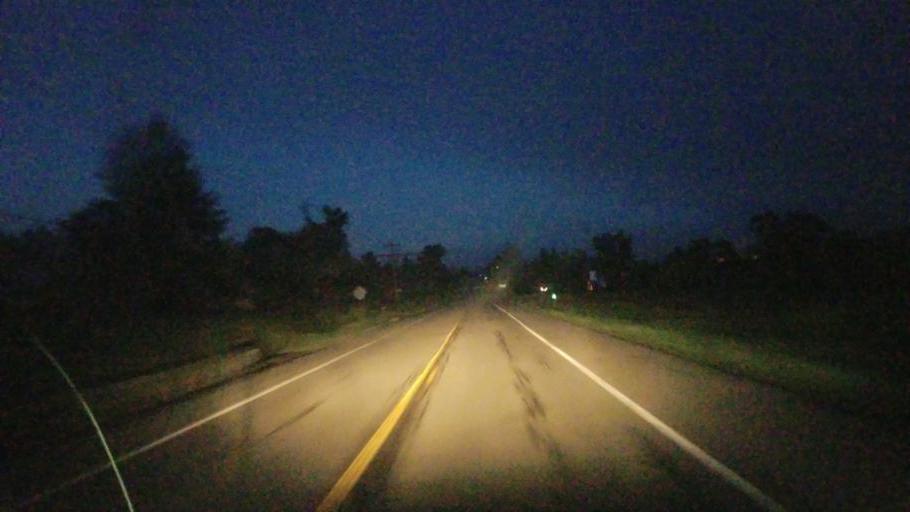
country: US
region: New York
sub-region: Allegany County
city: Wellsville
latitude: 42.0553
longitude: -77.9159
